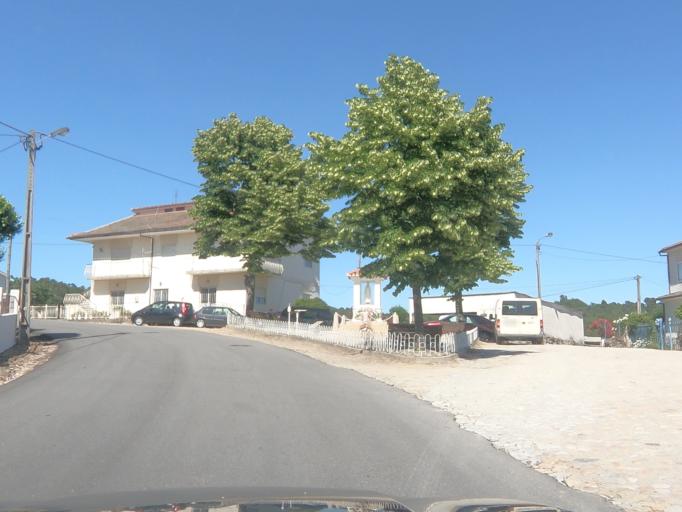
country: PT
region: Vila Real
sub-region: Vila Real
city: Vila Real
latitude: 41.2807
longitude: -7.6842
